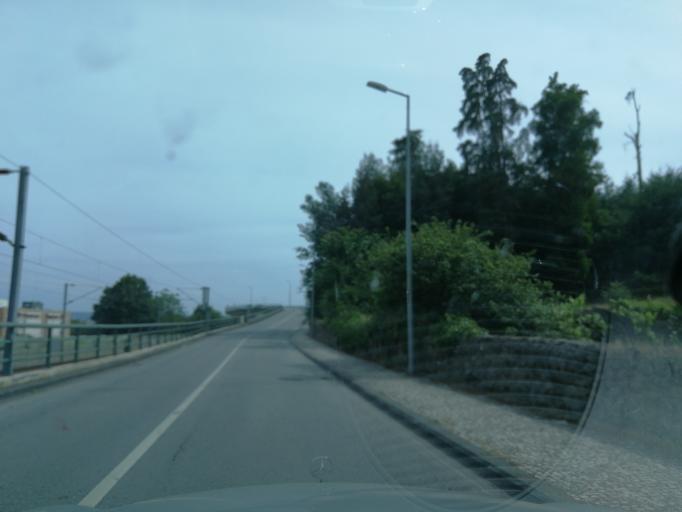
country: PT
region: Braga
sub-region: Vila Nova de Famalicao
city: Vila Nova de Famalicao
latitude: 41.4123
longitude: -8.5266
